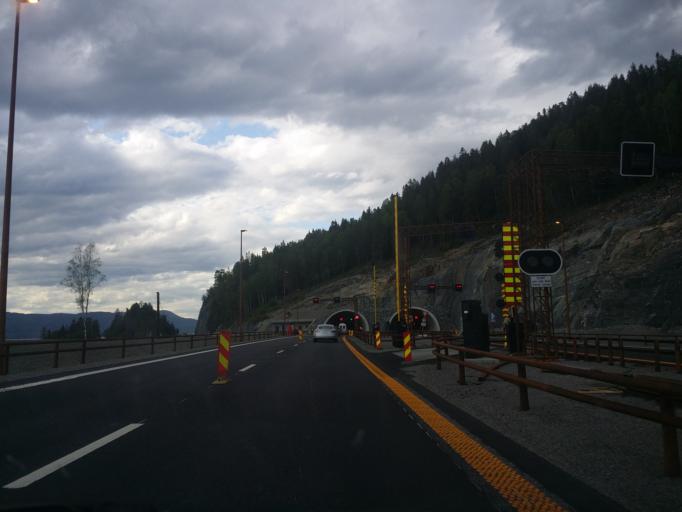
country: NO
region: Akershus
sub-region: Eidsvoll
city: Eidsvoll
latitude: 60.4314
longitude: 11.2406
